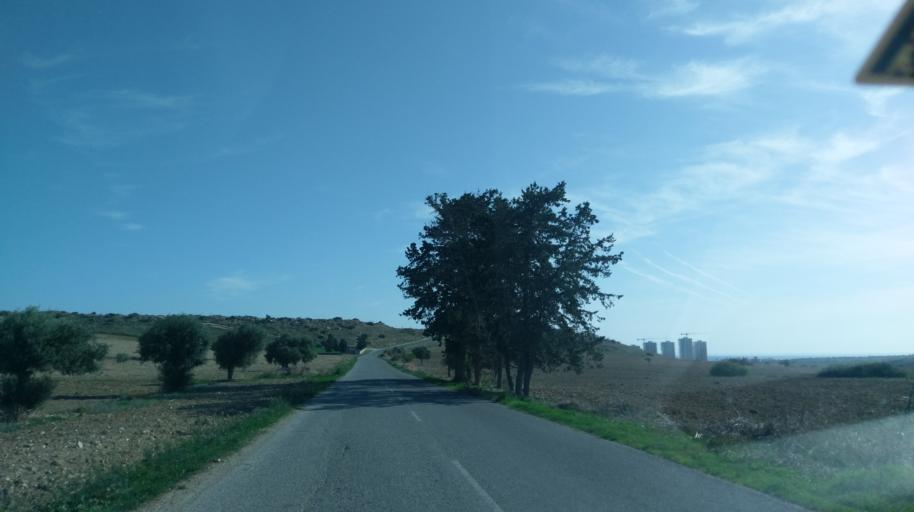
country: CY
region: Ammochostos
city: Trikomo
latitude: 35.3205
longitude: 33.9379
